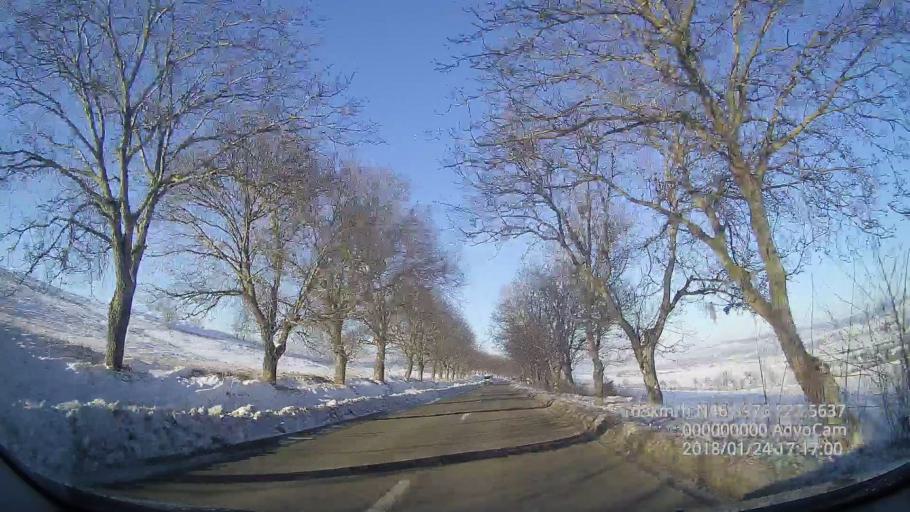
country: RO
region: Iasi
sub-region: Comuna Scanteia
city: Scanteia
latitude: 46.8984
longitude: 27.5637
